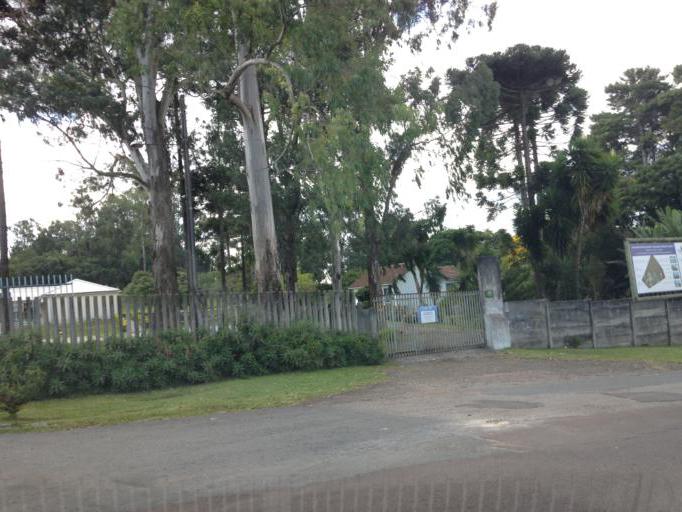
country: BR
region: Parana
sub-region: Pinhais
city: Pinhais
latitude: -25.4095
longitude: -49.2264
